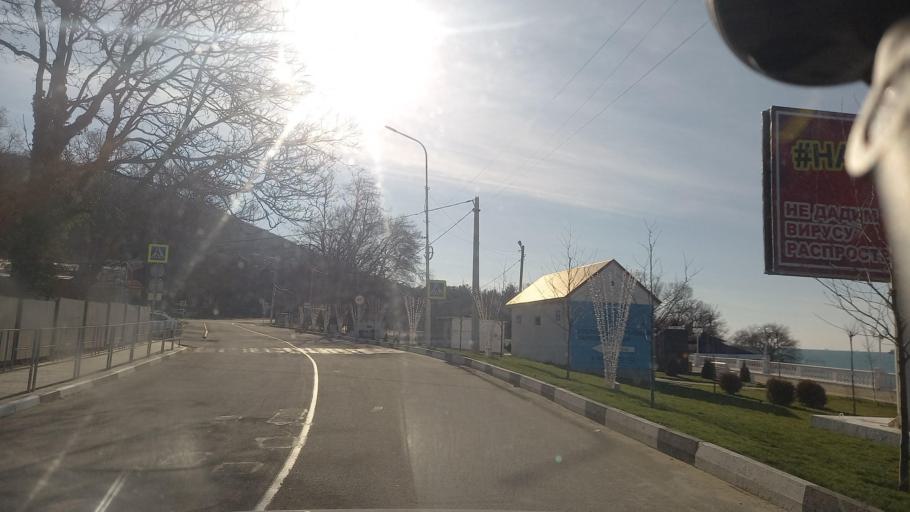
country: RU
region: Krasnodarskiy
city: Kabardinka
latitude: 44.6440
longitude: 37.9302
